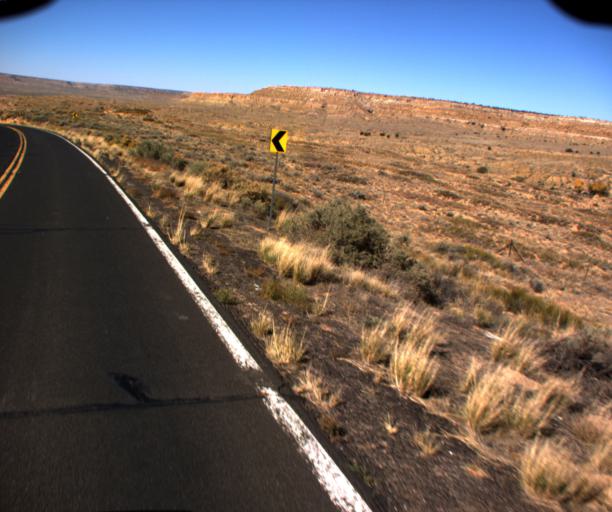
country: US
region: Arizona
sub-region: Navajo County
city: First Mesa
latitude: 35.8721
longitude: -110.5520
